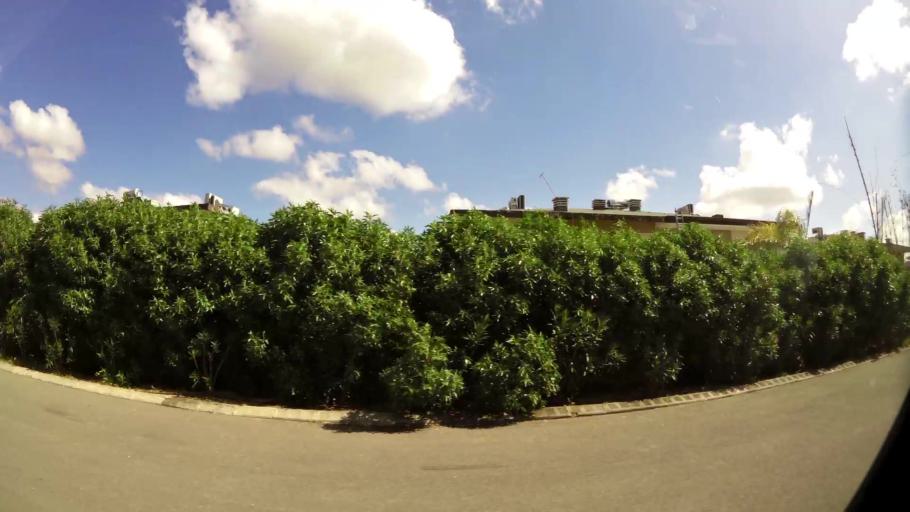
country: MA
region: Grand Casablanca
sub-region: Nouaceur
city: Bouskoura
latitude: 33.4718
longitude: -7.6097
